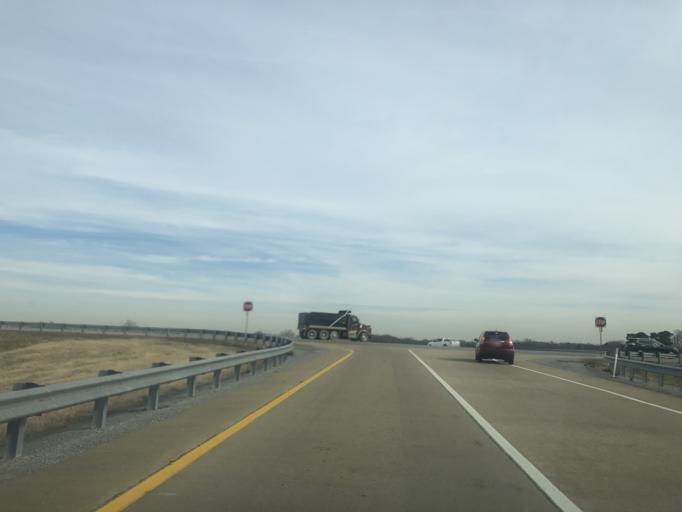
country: US
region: Tennessee
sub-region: Rutherford County
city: Smyrna
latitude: 35.8652
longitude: -86.5107
